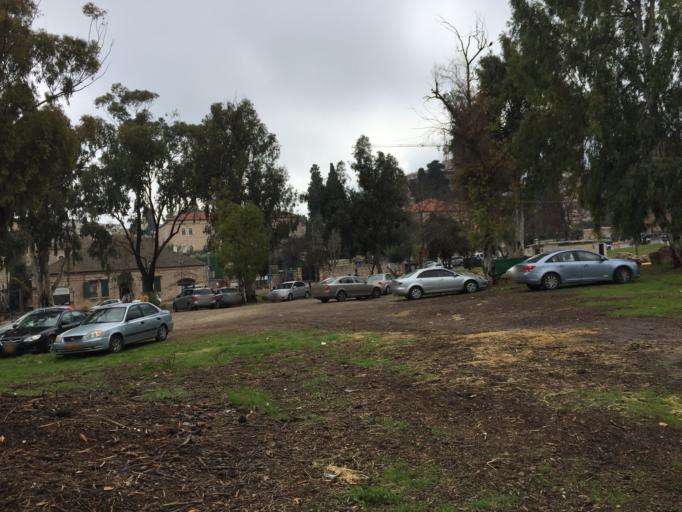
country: IL
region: Jerusalem
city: West Jerusalem
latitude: 31.7777
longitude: 35.2201
